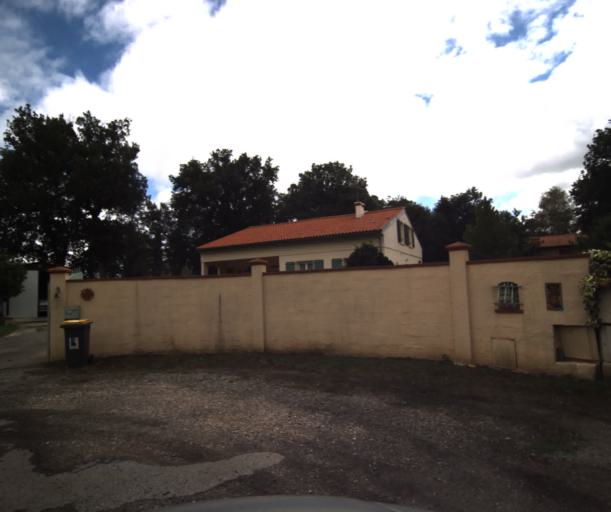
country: FR
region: Midi-Pyrenees
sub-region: Departement de la Haute-Garonne
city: Roquettes
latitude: 43.4923
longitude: 1.3832
